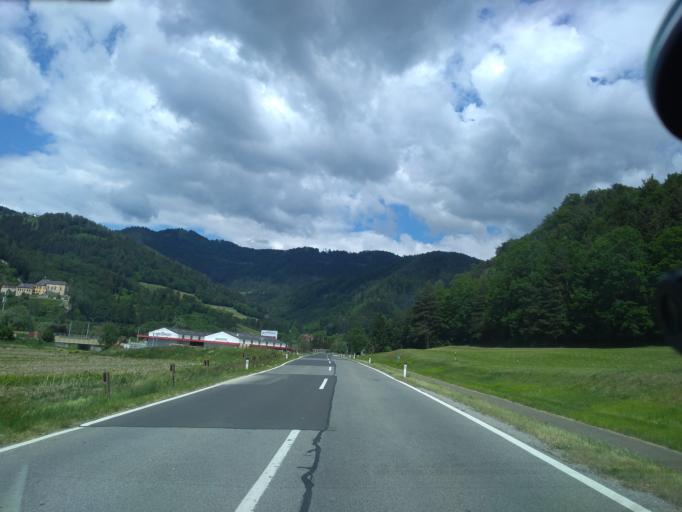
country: AT
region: Styria
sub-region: Politischer Bezirk Graz-Umgebung
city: Frohnleiten
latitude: 47.2460
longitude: 15.3204
